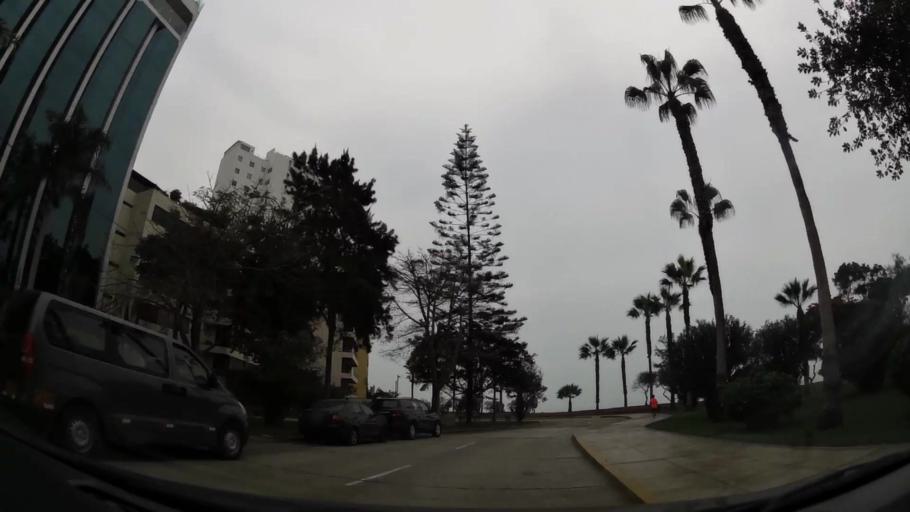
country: PE
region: Lima
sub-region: Lima
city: Surco
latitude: -12.1351
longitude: -77.0276
